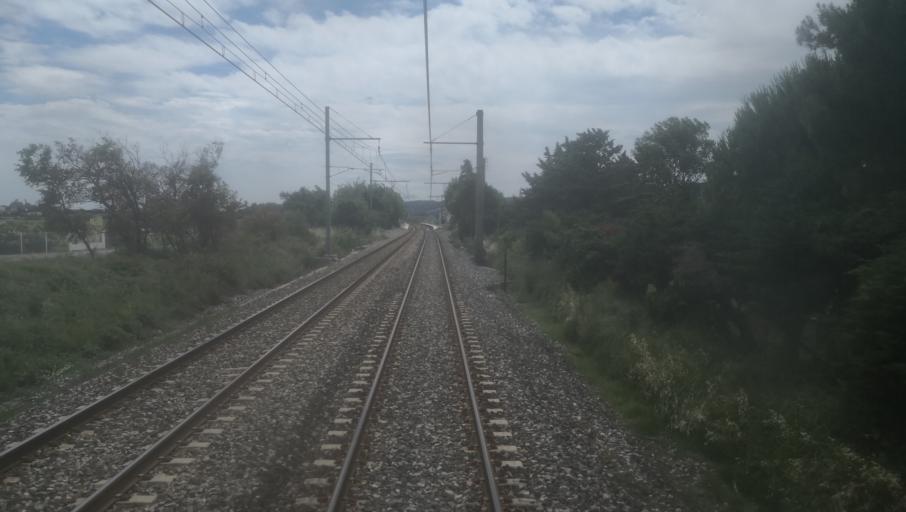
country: FR
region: Languedoc-Roussillon
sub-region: Departement de l'Herault
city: Mireval
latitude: 43.5020
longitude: 3.8012
